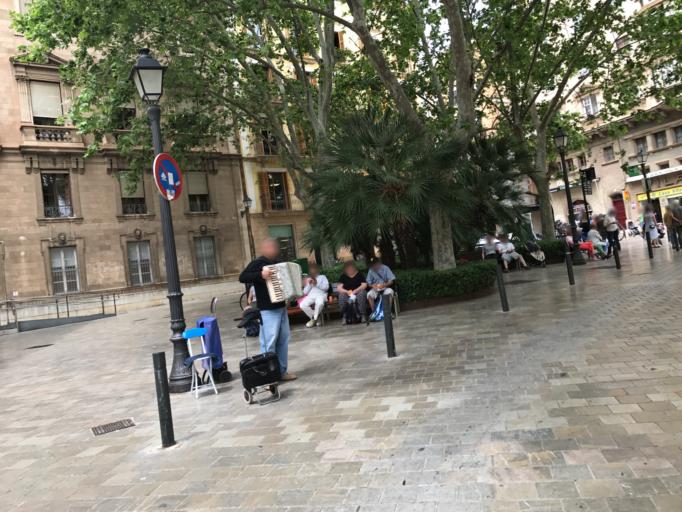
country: ES
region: Balearic Islands
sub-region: Illes Balears
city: Palma
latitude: 39.5689
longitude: 2.6508
